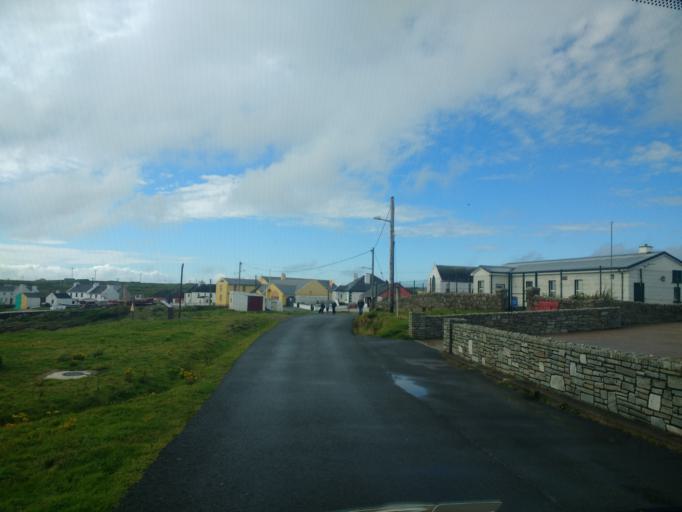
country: IE
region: Ulster
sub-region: County Donegal
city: Derrybeg
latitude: 55.2646
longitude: -8.2241
